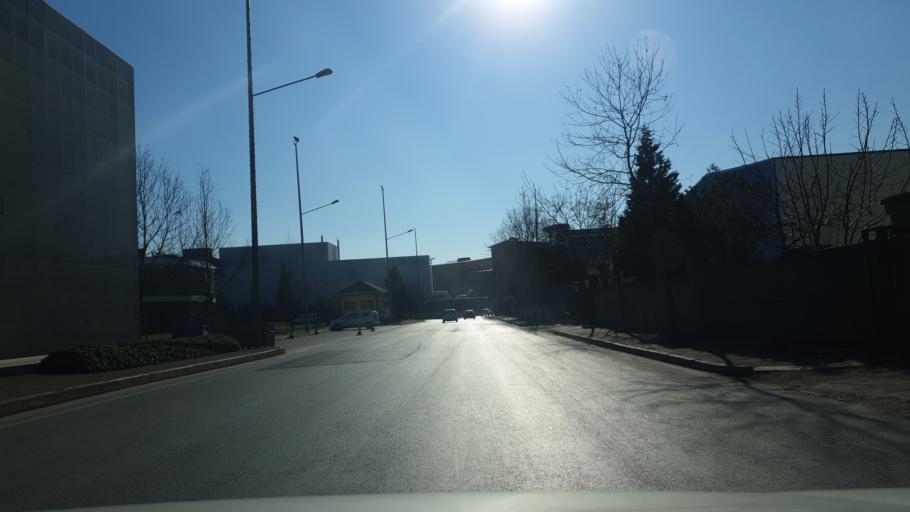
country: TR
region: Kocaeli
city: Balcik
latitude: 40.8784
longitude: 29.3662
